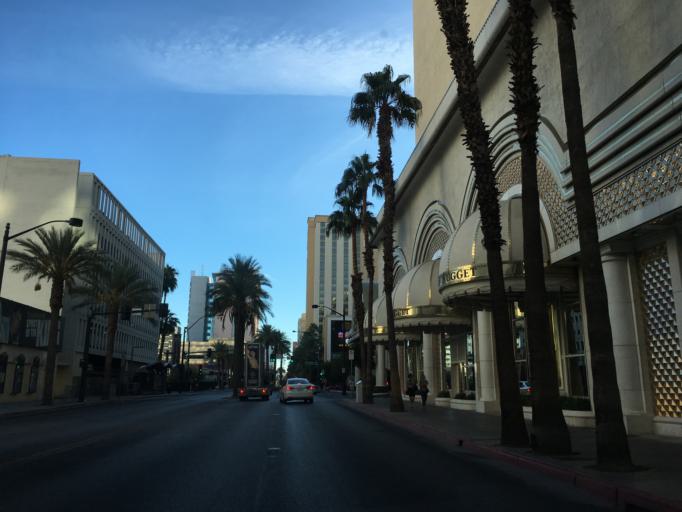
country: US
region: Nevada
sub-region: Clark County
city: Las Vegas
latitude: 36.1705
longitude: -115.1443
